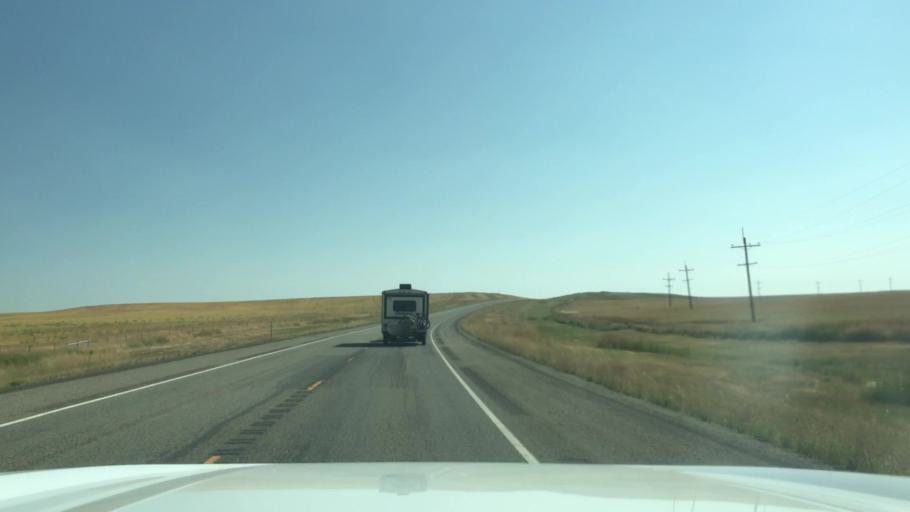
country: US
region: Montana
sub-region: Wheatland County
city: Harlowton
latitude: 46.4740
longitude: -109.7662
